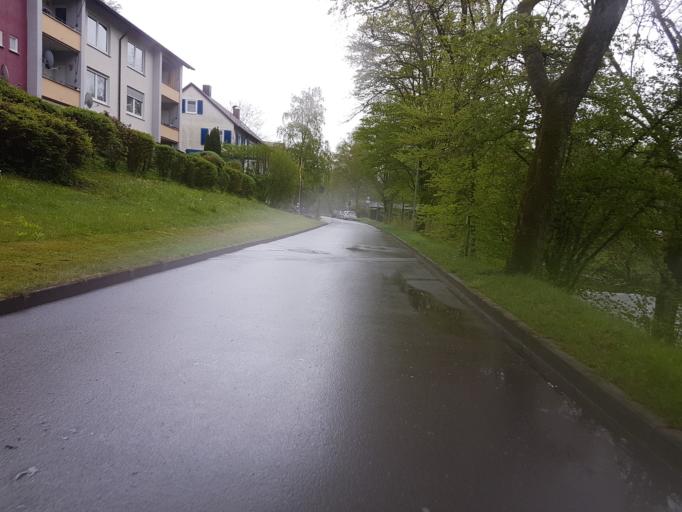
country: DE
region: Baden-Wuerttemberg
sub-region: Freiburg Region
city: Oberndorf
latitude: 48.2869
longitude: 8.5813
